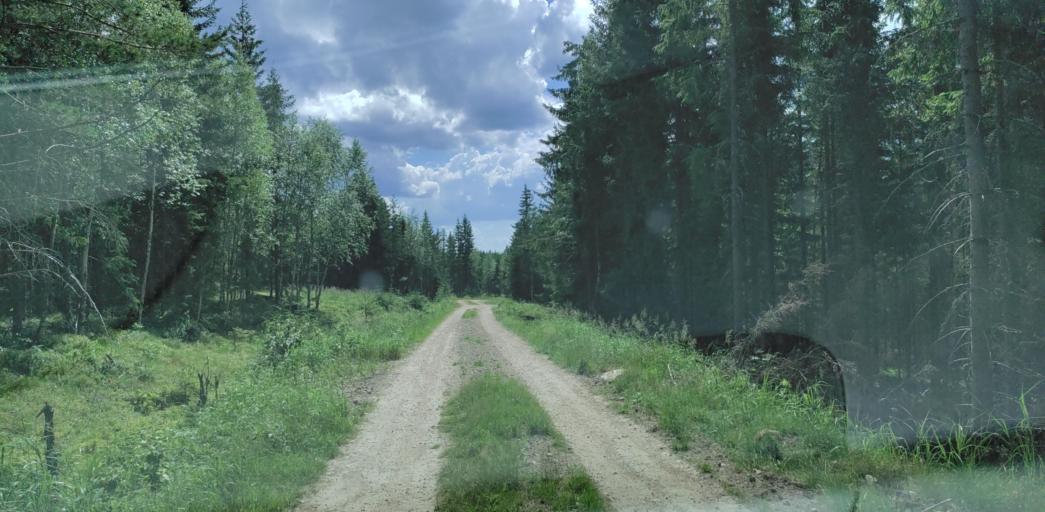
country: SE
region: Vaermland
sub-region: Hagfors Kommun
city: Ekshaerad
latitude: 60.0638
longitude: 13.3393
